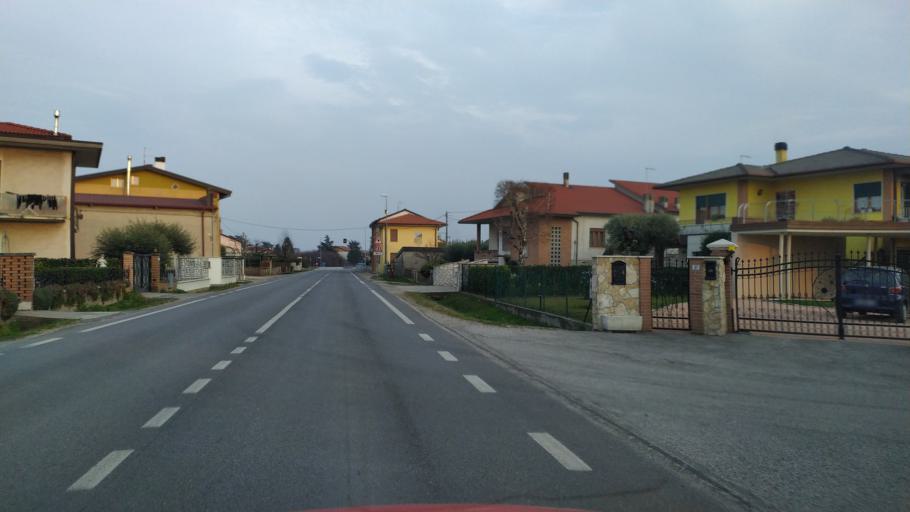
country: IT
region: Veneto
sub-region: Provincia di Vicenza
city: Preara-Moraro-Leva Nord
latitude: 45.6811
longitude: 11.5406
